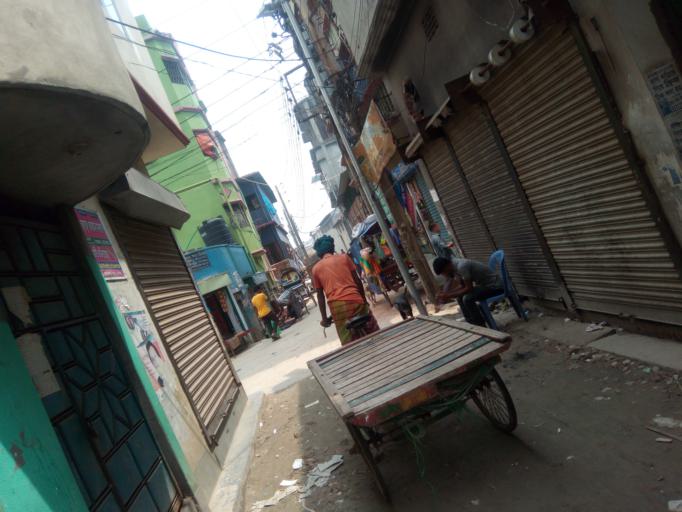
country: BD
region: Dhaka
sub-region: Dhaka
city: Dhaka
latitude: 23.6876
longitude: 90.4377
